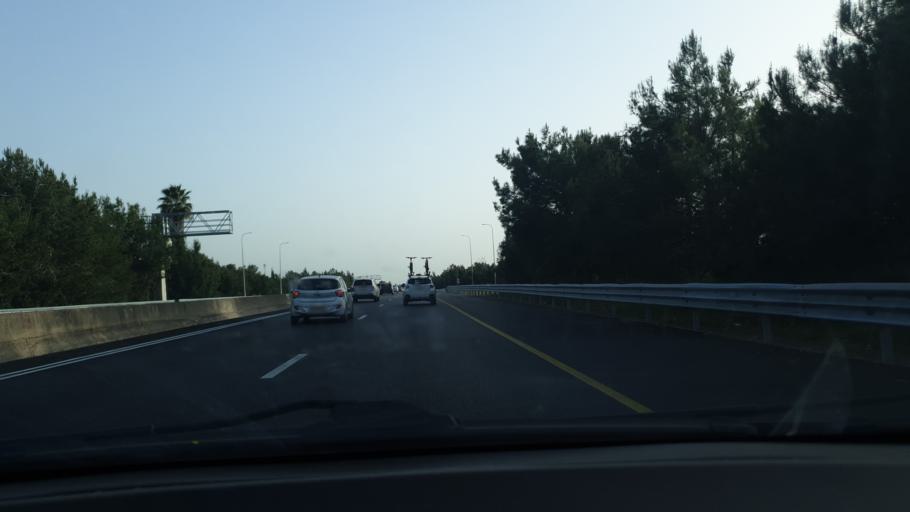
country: IL
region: Central District
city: Even Yehuda
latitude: 32.2345
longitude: 34.8847
